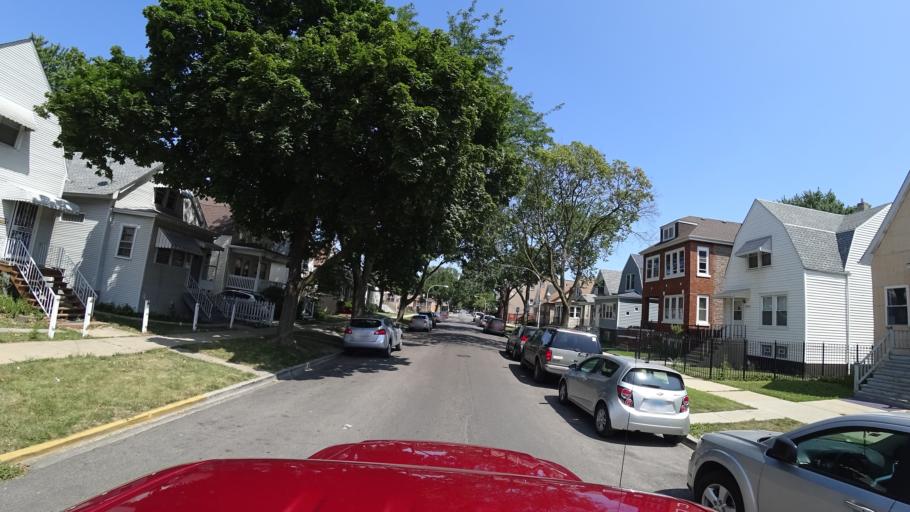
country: US
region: Illinois
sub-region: Cook County
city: Chicago
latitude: 41.8202
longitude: -87.6872
